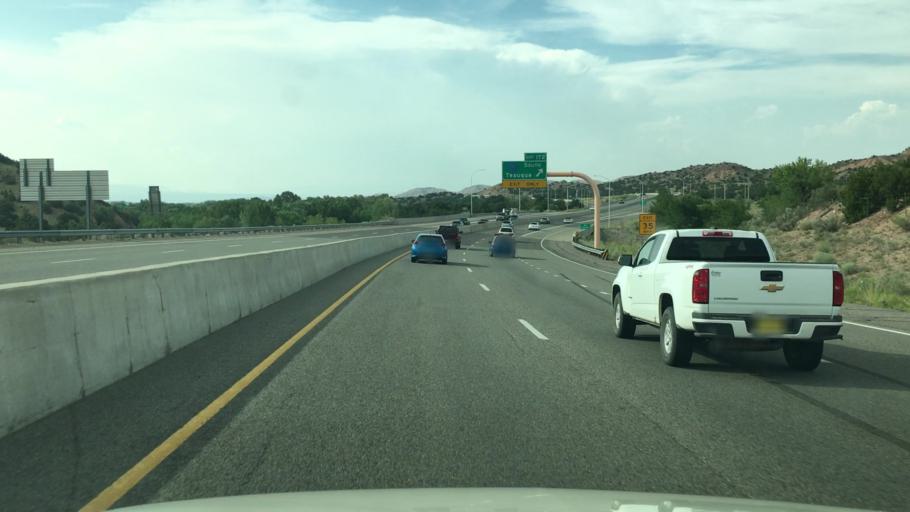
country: US
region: New Mexico
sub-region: Santa Fe County
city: Santa Fe
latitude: 35.7785
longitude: -105.9473
